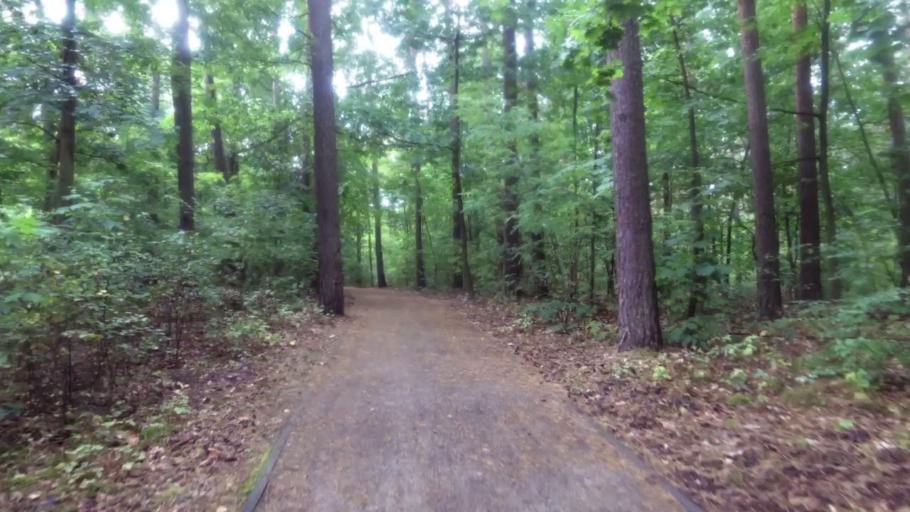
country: PL
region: West Pomeranian Voivodeship
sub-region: Powiat mysliborski
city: Debno
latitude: 52.7131
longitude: 14.6928
